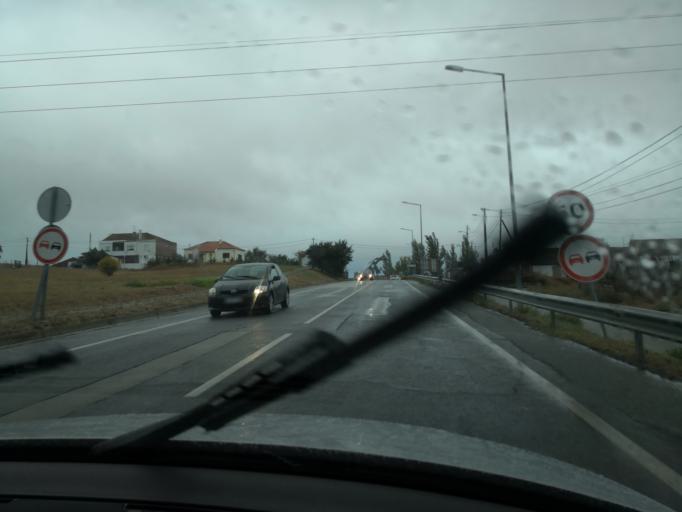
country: PT
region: Setubal
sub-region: Moita
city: Moita
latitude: 38.6457
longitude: -8.9804
